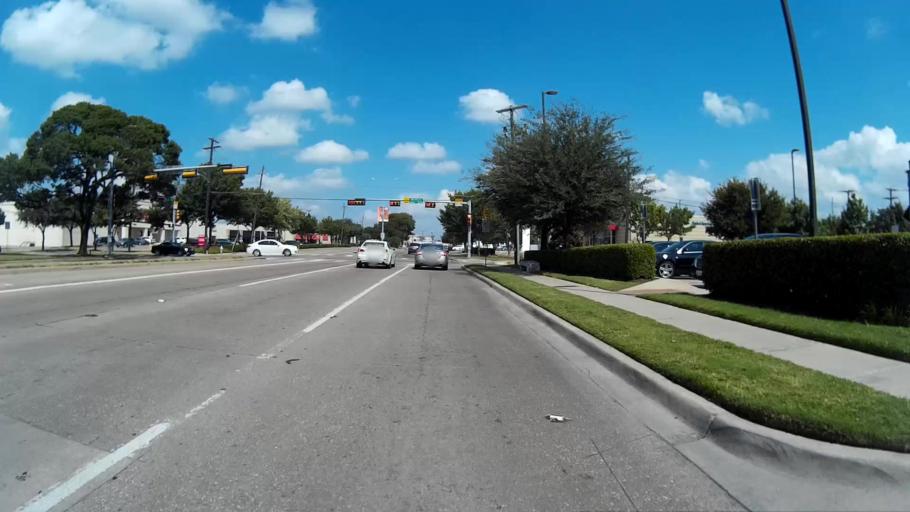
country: US
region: Texas
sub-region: Dallas County
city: Highland Park
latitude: 32.8484
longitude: -96.7700
